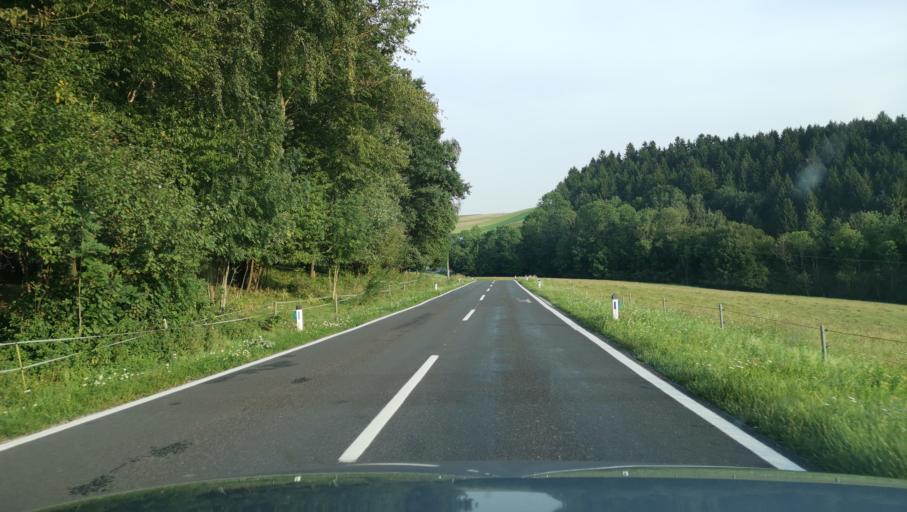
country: DE
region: Bavaria
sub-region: Lower Bavaria
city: Obernzell
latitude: 48.3666
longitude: 13.6661
